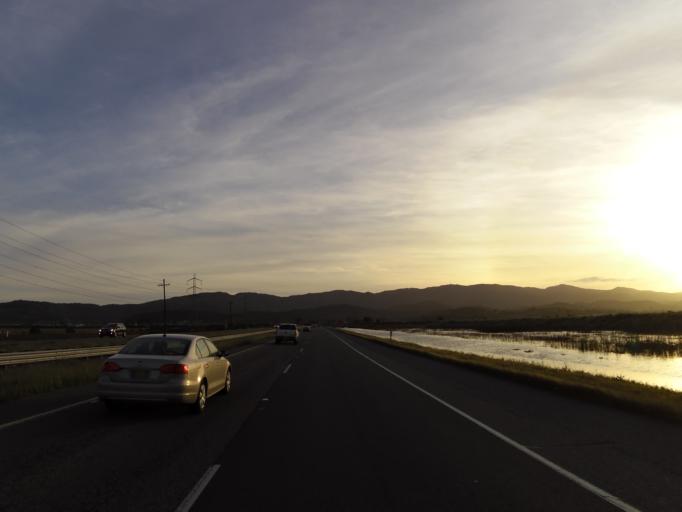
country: US
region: California
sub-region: Marin County
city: Black Point-Green Point
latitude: 38.0917
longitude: -122.5292
